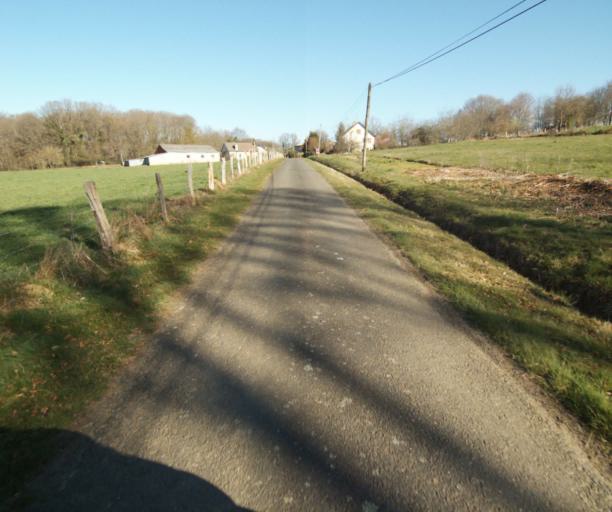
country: FR
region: Limousin
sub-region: Departement de la Correze
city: Saint-Clement
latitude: 45.3816
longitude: 1.6534
